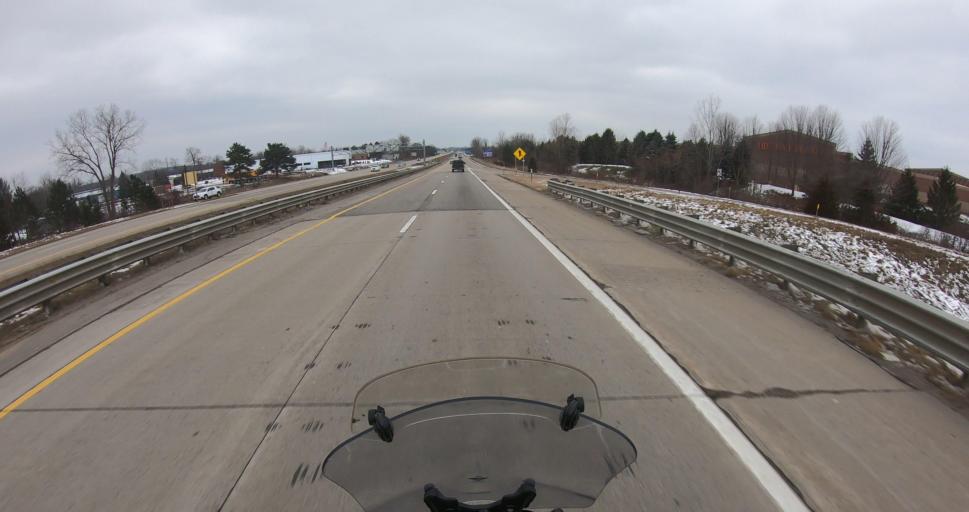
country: US
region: Michigan
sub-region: Genesee County
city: Fenton
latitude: 42.8008
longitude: -83.7295
